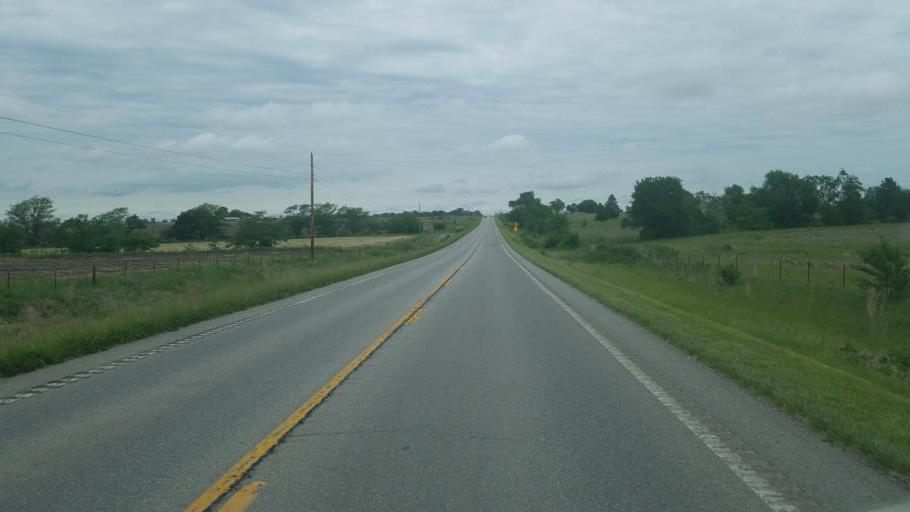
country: US
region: Missouri
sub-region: Morgan County
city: Versailles
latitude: 38.4506
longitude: -92.8093
